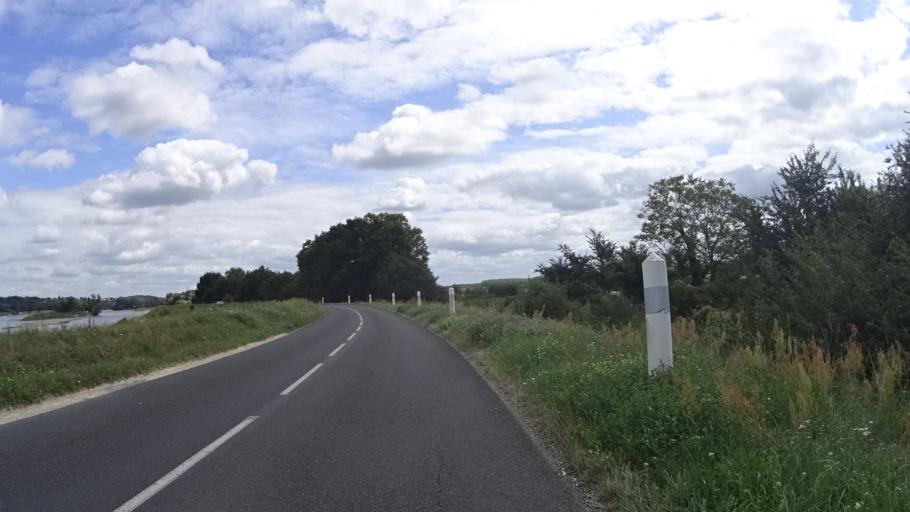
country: FR
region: Centre
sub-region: Departement d'Indre-et-Loire
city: Langeais
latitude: 47.2985
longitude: 0.3665
